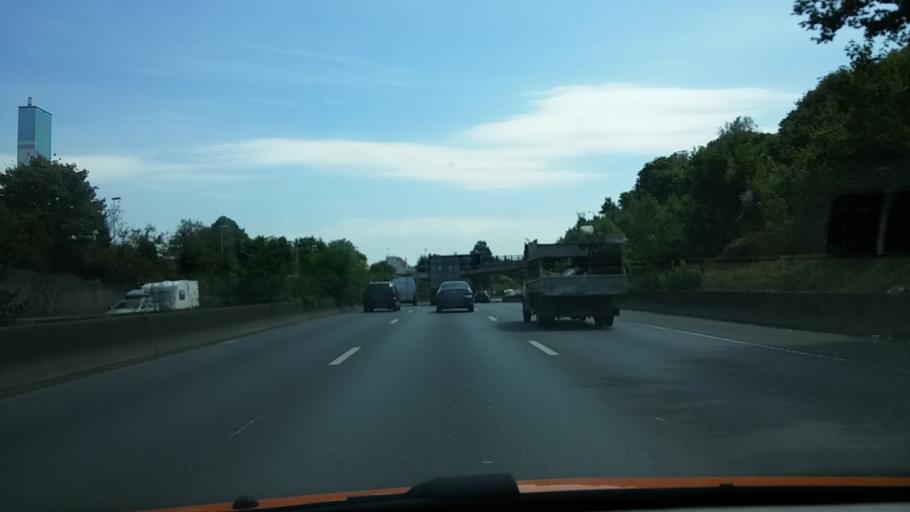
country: FR
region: Ile-de-France
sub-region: Departement du Val-de-Marne
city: Fontenay-sous-Bois
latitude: 48.8725
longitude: 2.4806
